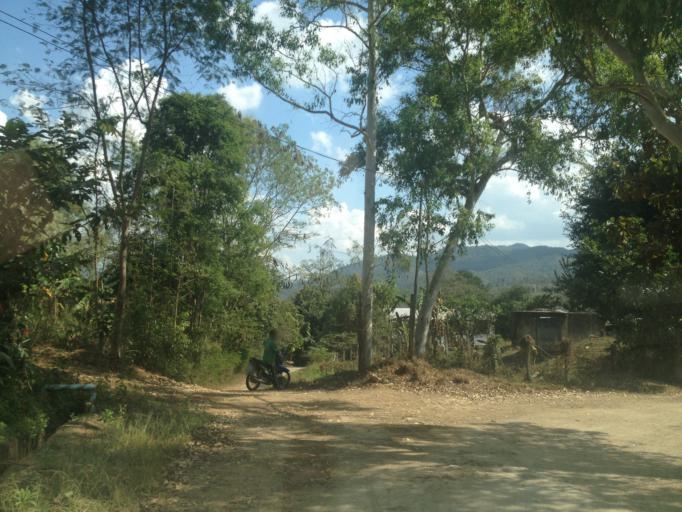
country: TH
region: Mae Hong Son
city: Ban Huai I Huak
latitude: 18.0903
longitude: 98.1950
